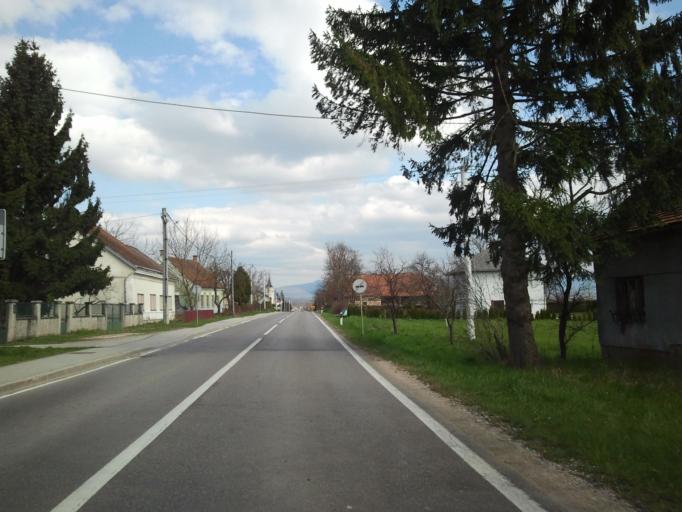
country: HR
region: Zagrebacka
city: Jastrebarsko
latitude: 45.6041
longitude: 15.5983
